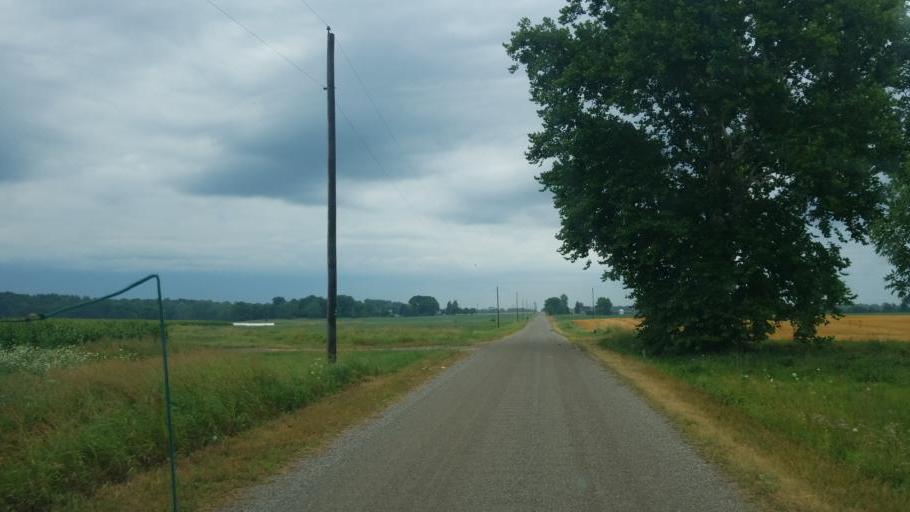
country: US
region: Indiana
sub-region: DeKalb County
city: Butler
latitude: 41.4429
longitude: -84.9029
